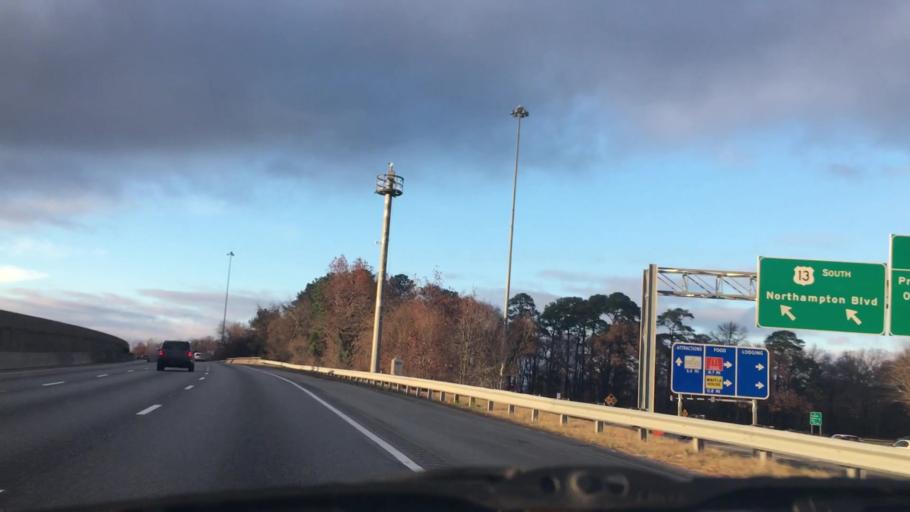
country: US
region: Virginia
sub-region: City of Norfolk
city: Norfolk
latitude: 36.8739
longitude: -76.1964
